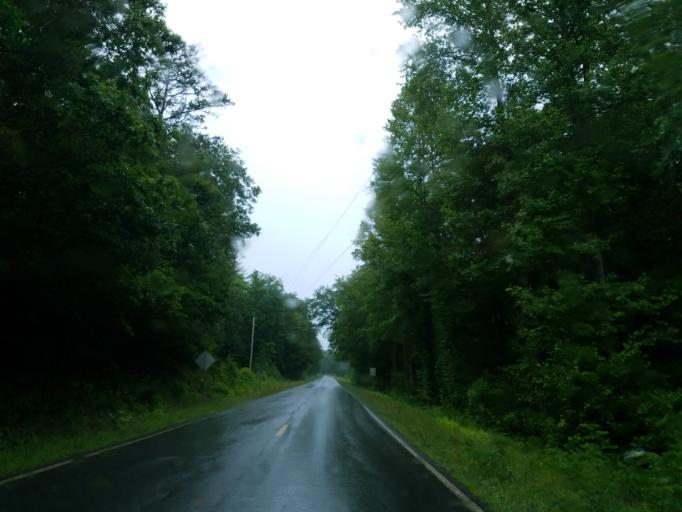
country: US
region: Georgia
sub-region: Fannin County
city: Blue Ridge
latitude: 34.7873
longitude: -84.2536
